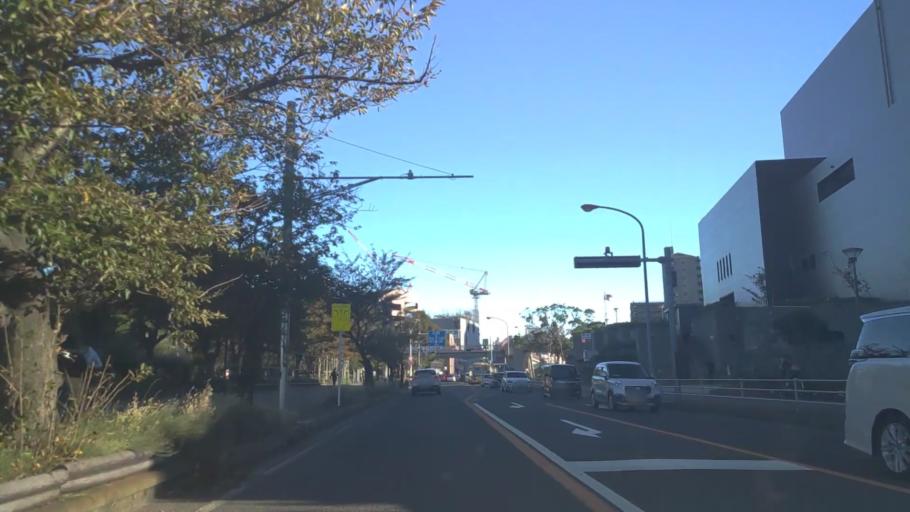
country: JP
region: Kanagawa
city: Chigasaki
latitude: 35.3358
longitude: 139.4043
